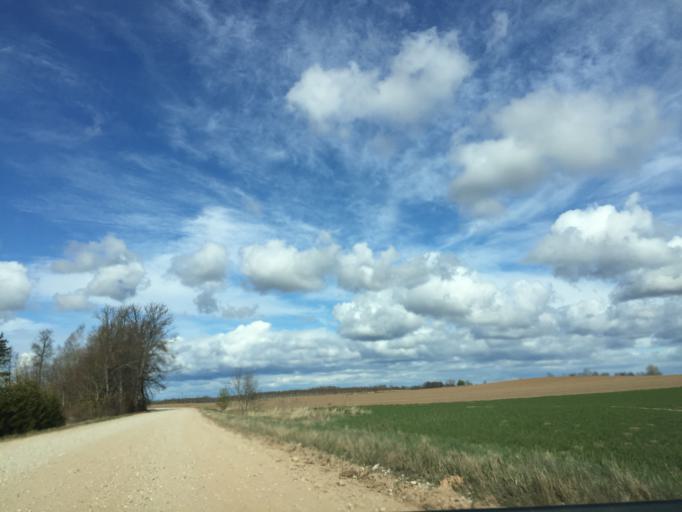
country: LV
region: Limbazu Rajons
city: Limbazi
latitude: 57.5813
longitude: 24.5965
